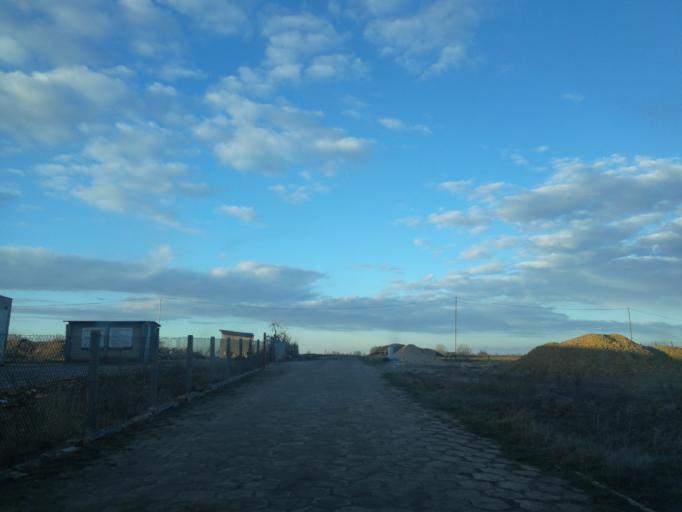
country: PL
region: Kujawsko-Pomorskie
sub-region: Powiat torunski
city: Chelmza
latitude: 53.1883
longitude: 18.6304
